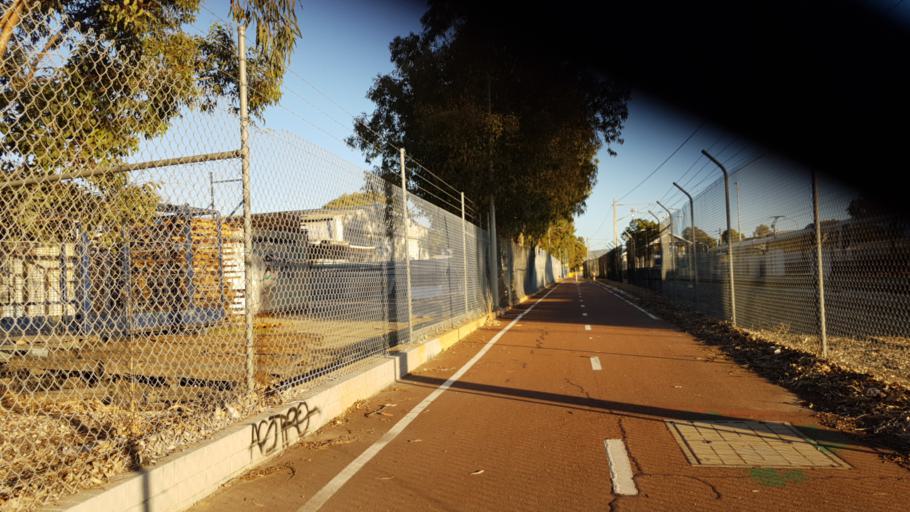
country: AU
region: Western Australia
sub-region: Gosnells
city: Maddington
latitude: -32.0486
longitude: 115.9818
